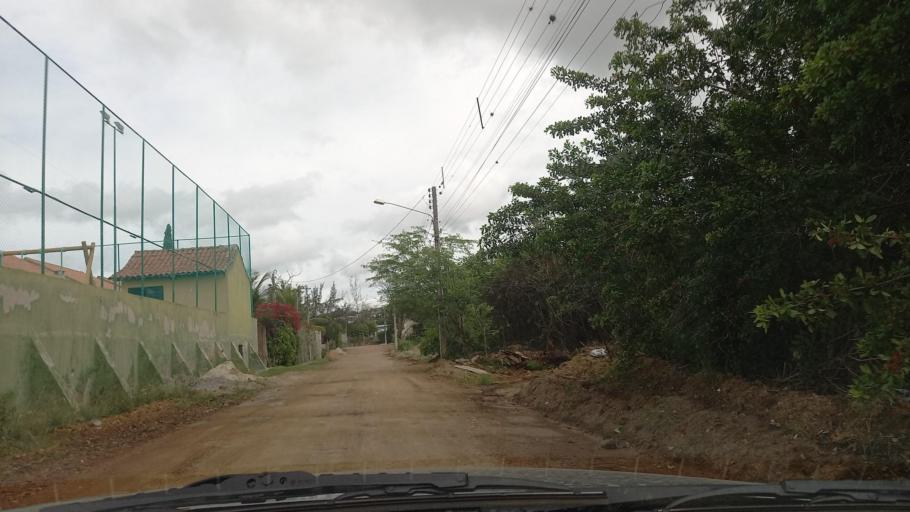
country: BR
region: Pernambuco
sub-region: Gravata
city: Gravata
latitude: -8.1898
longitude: -35.5846
